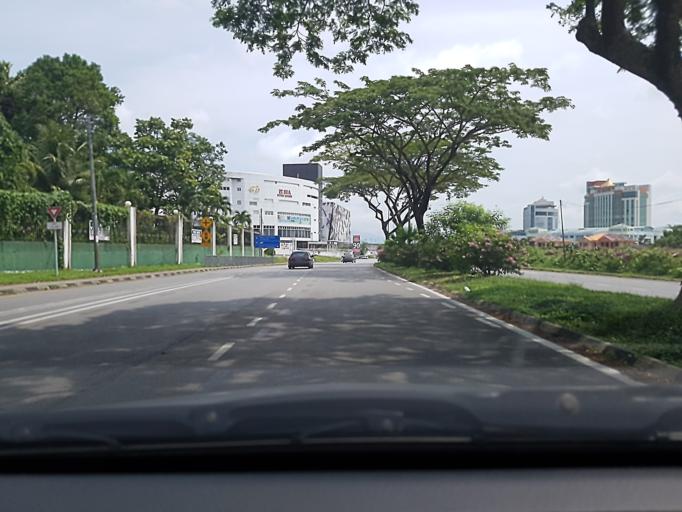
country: MY
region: Sarawak
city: Kuching
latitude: 1.5198
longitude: 110.3578
